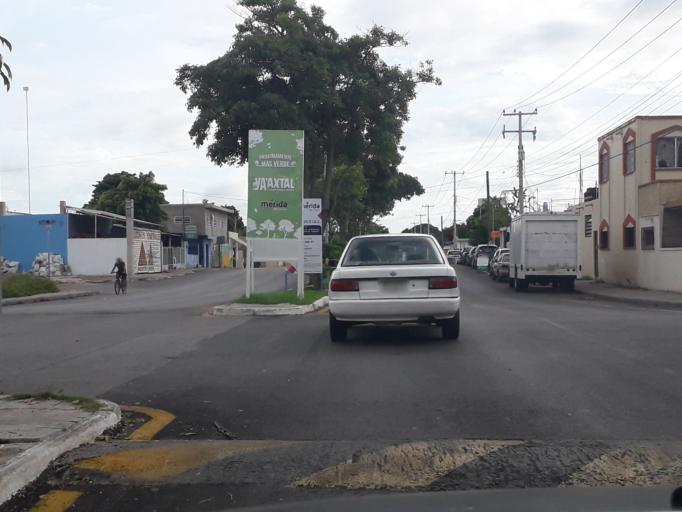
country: MX
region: Yucatan
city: Merida
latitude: 20.9678
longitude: -89.6636
